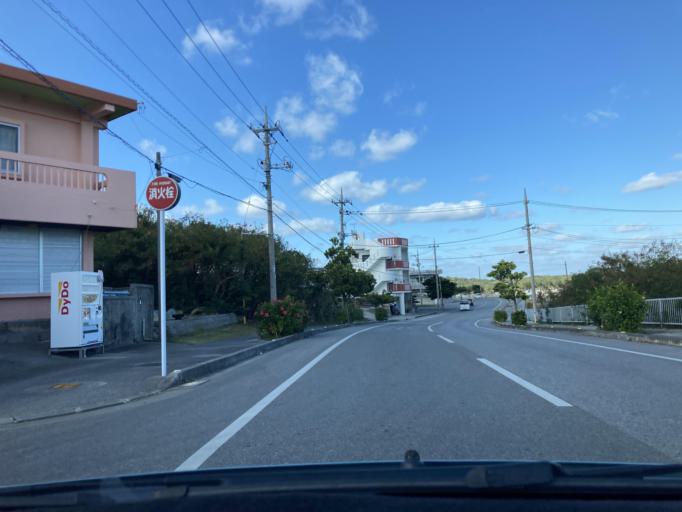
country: JP
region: Okinawa
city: Katsuren-haebaru
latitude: 26.3079
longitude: 127.9205
